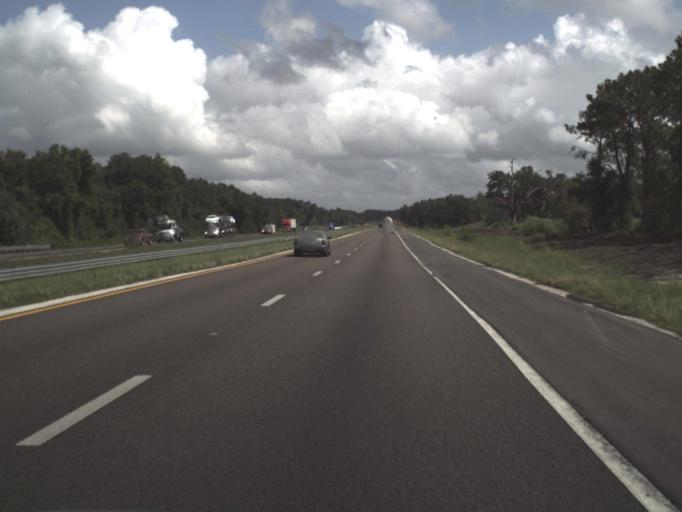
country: US
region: Florida
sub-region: Pasco County
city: San Antonio
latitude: 28.3760
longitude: -82.3193
